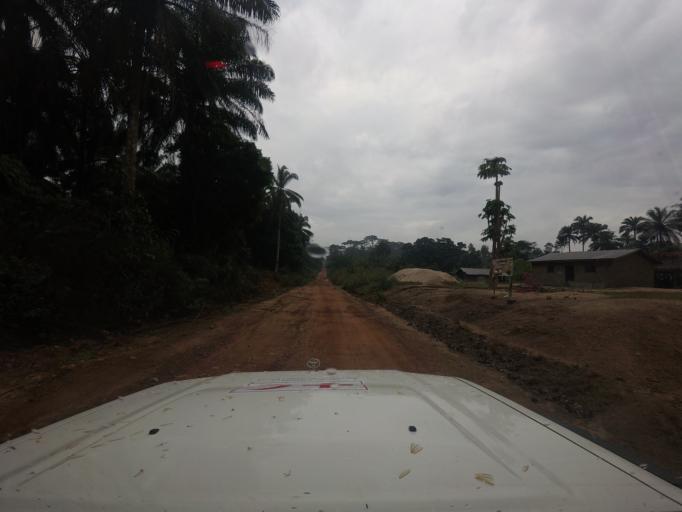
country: LR
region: Lofa
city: Voinjama
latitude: 8.3871
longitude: -9.8235
